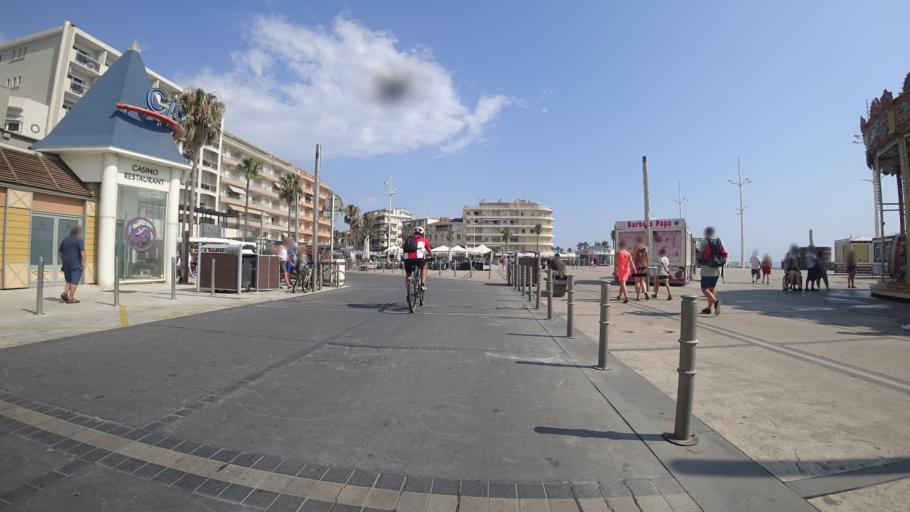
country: FR
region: Languedoc-Roussillon
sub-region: Departement des Pyrenees-Orientales
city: Canet-en-Roussillon
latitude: 42.6926
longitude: 3.0353
